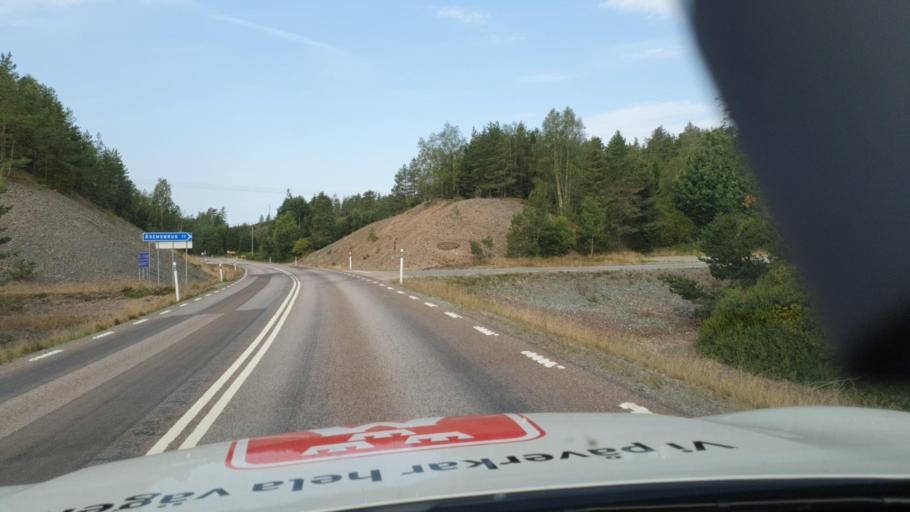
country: SE
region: Vaestra Goetaland
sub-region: Melleruds Kommun
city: Mellerud
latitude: 58.7501
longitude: 12.3315
